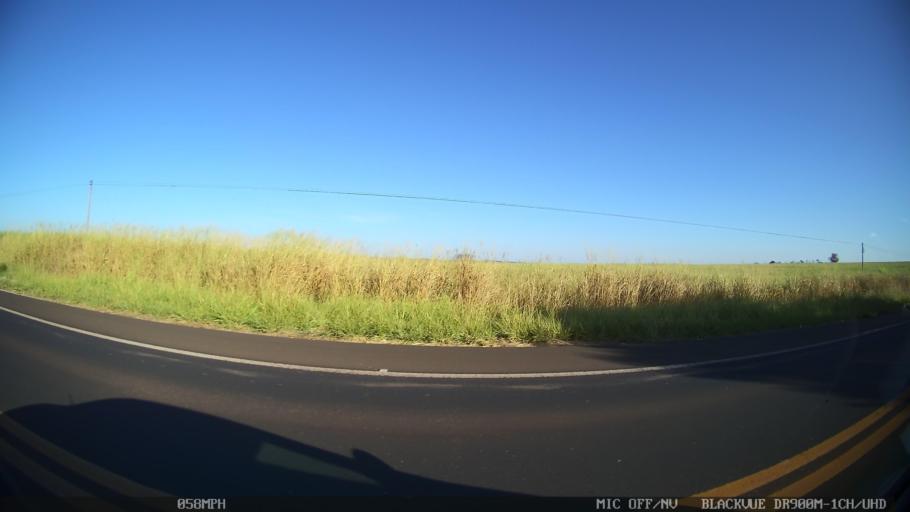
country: BR
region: Sao Paulo
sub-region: Olimpia
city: Olimpia
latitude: -20.7252
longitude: -49.0337
